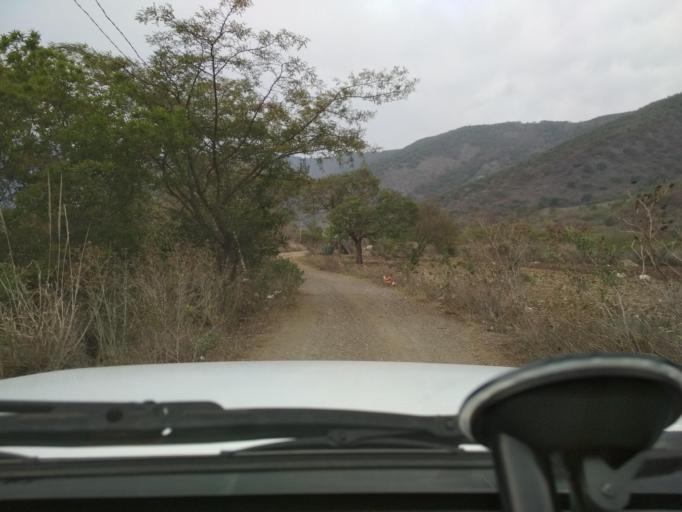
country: MX
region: Veracruz
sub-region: Nogales
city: Taza de Agua Ojo Zarco
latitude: 18.7904
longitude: -97.2161
